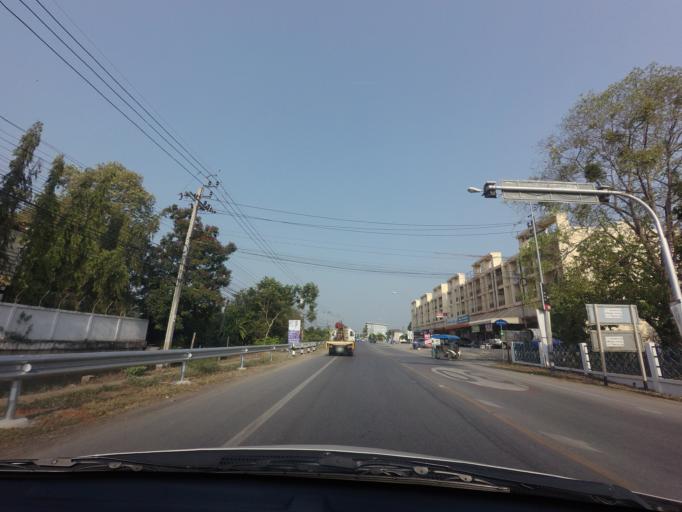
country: TH
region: Bangkok
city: Thawi Watthana
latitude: 13.8115
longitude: 100.3488
